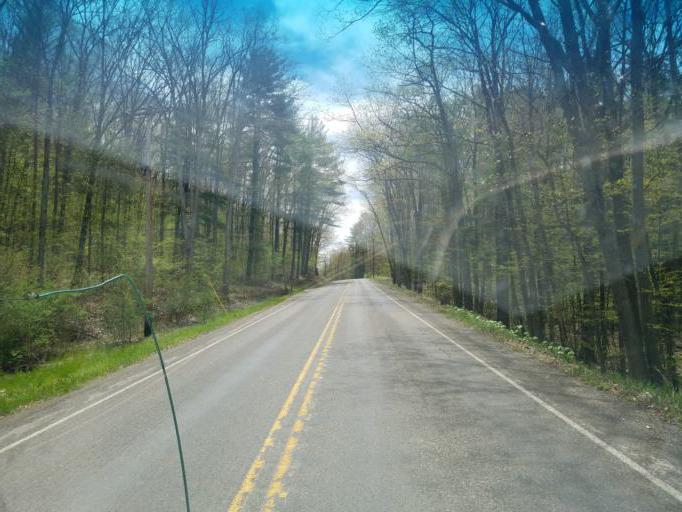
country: US
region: Pennsylvania
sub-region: Tioga County
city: Wellsboro
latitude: 41.7320
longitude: -77.4263
